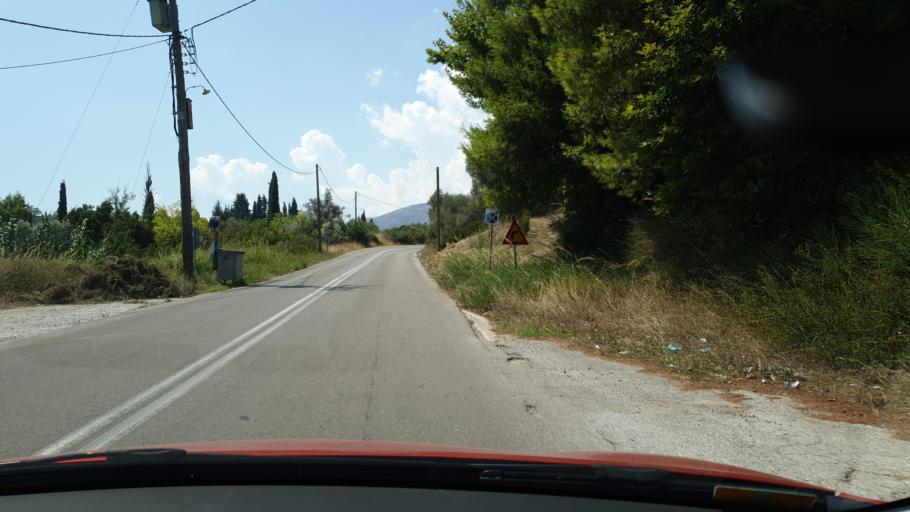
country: GR
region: Central Greece
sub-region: Nomos Evvoias
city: Oxilithos
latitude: 38.5845
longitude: 24.0645
